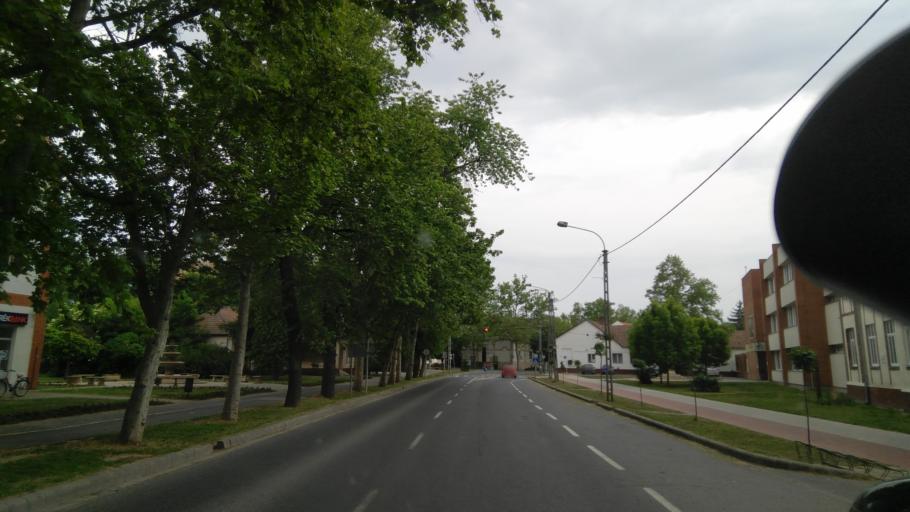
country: HU
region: Bekes
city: Sarkad
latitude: 46.7448
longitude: 21.3835
